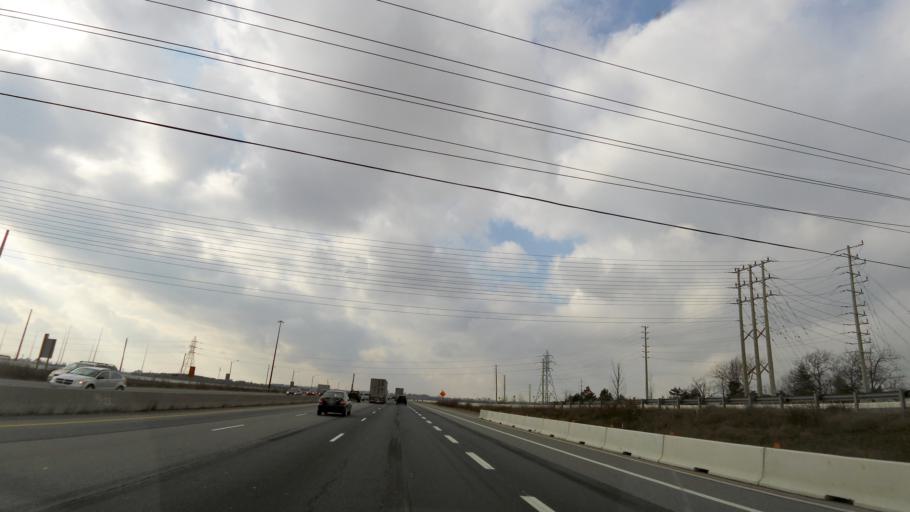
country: CA
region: Ontario
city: Cambridge
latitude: 43.4141
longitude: -80.3299
